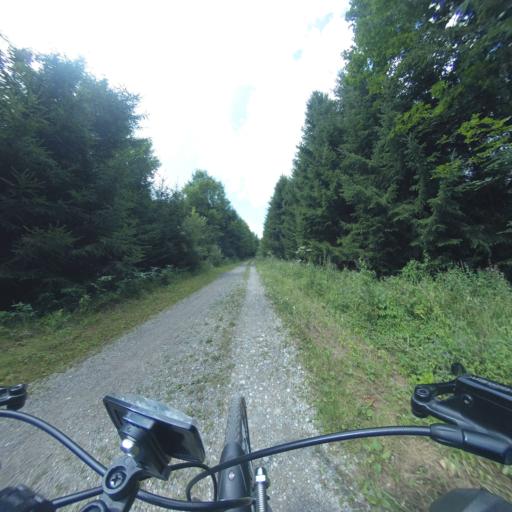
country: DE
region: Bavaria
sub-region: Upper Bavaria
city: Gauting
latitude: 48.0926
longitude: 11.3375
